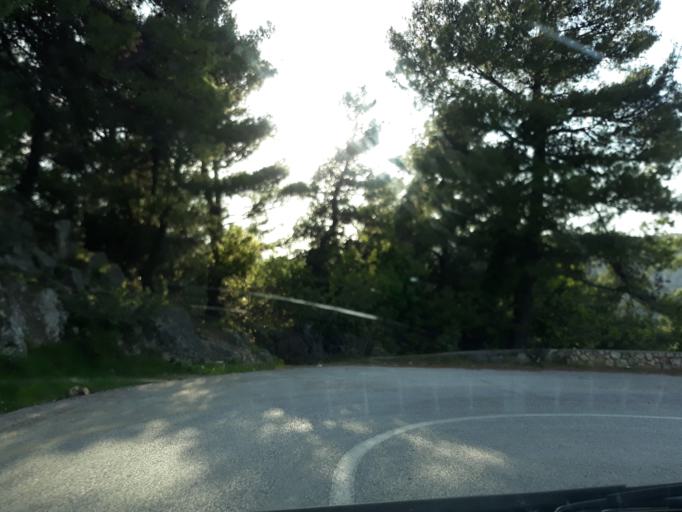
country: GR
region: Attica
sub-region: Nomarchia Anatolikis Attikis
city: Afidnes
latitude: 38.2227
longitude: 23.7805
